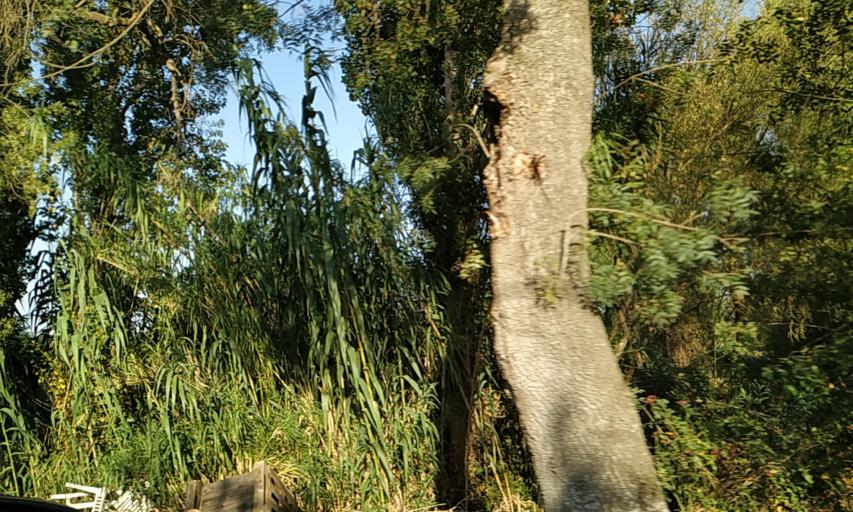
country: PT
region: Santarem
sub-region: Santarem
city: Santarem
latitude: 39.2571
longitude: -8.6700
